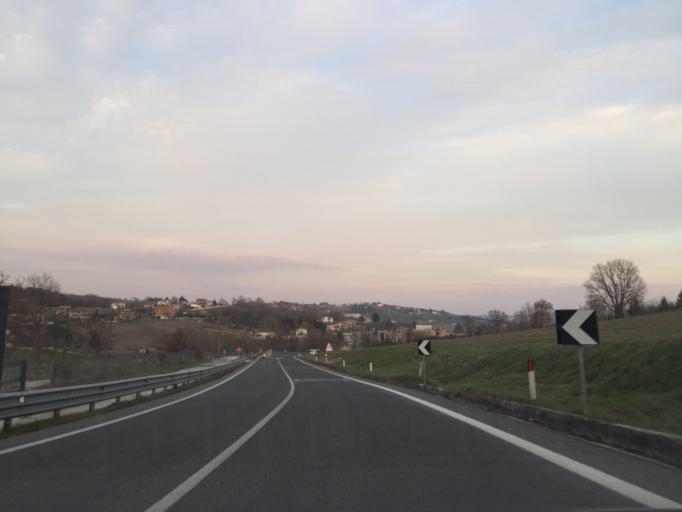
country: IT
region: Molise
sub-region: Provincia di Campobasso
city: Campobasso
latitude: 41.5567
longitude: 14.7025
